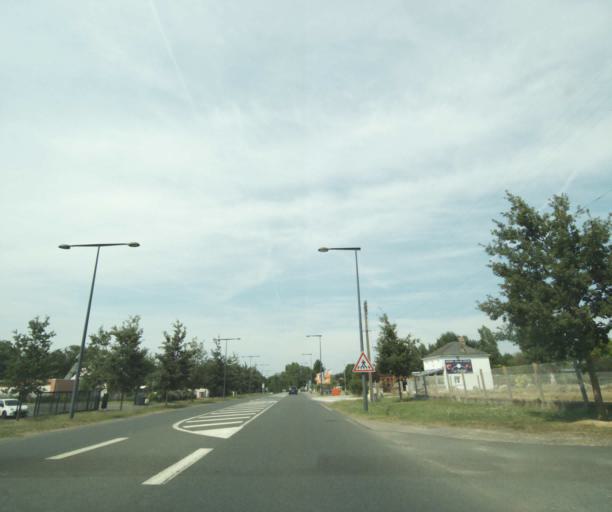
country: FR
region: Centre
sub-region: Departement d'Indre-et-Loire
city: Montbazon
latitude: 47.2779
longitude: 0.7104
